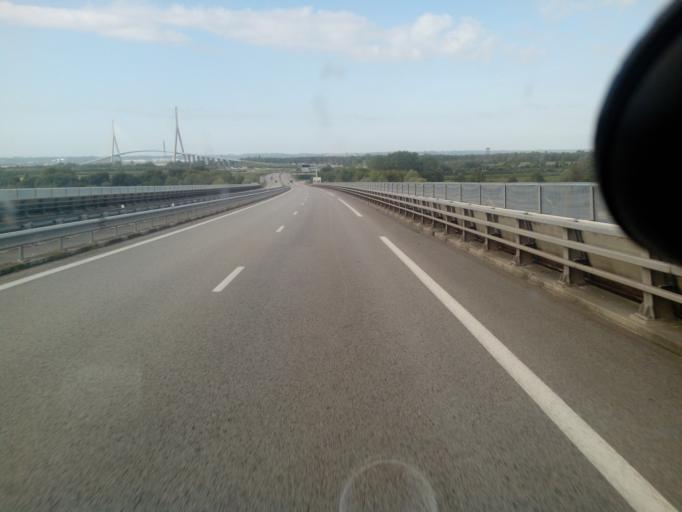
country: FR
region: Lower Normandy
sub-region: Departement du Calvados
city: La Riviere-Saint-Sauveur
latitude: 49.4070
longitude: 0.2660
